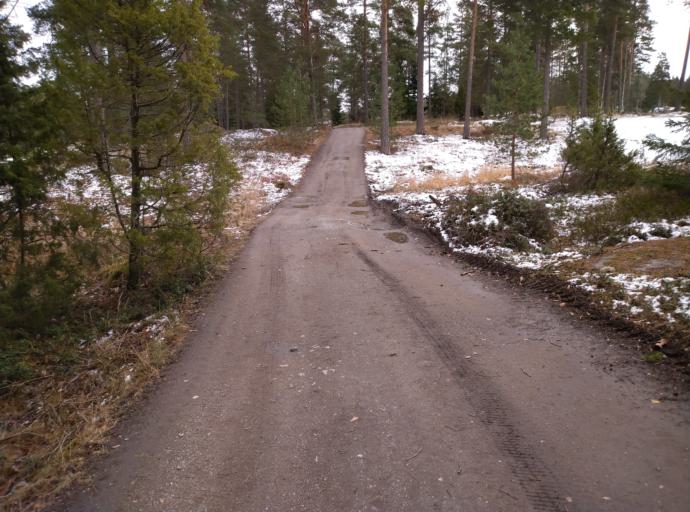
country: SE
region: Stockholm
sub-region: Nacka Kommun
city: Fisksatra
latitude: 59.2870
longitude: 18.2395
